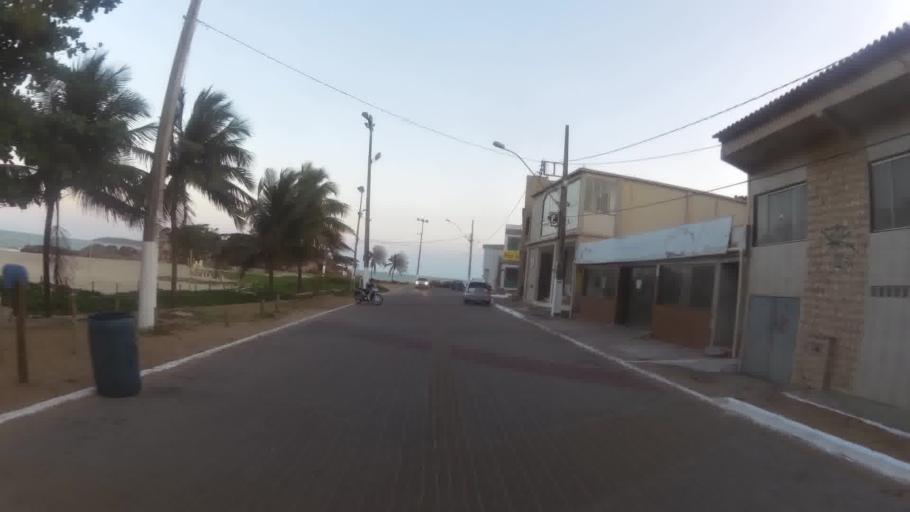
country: BR
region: Espirito Santo
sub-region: Piuma
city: Piuma
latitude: -20.9037
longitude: -40.7775
